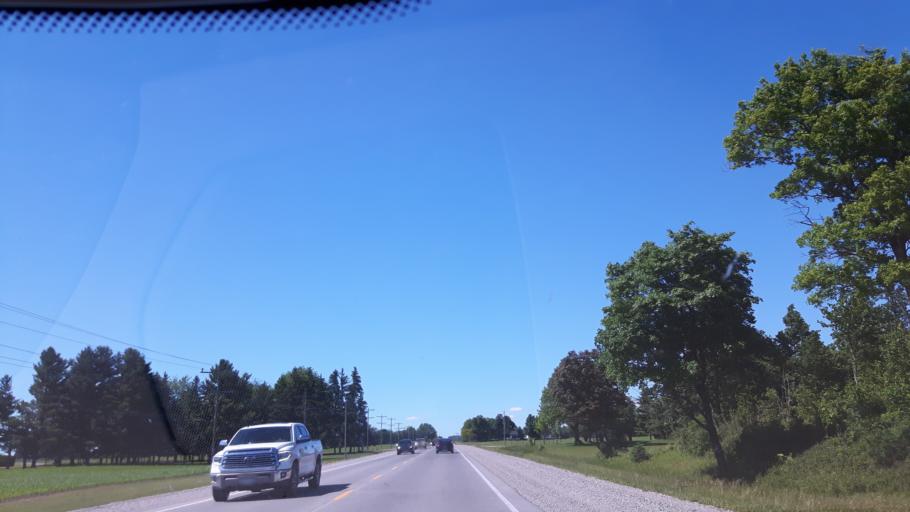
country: CA
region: Ontario
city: London
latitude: 43.0902
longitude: -81.3153
